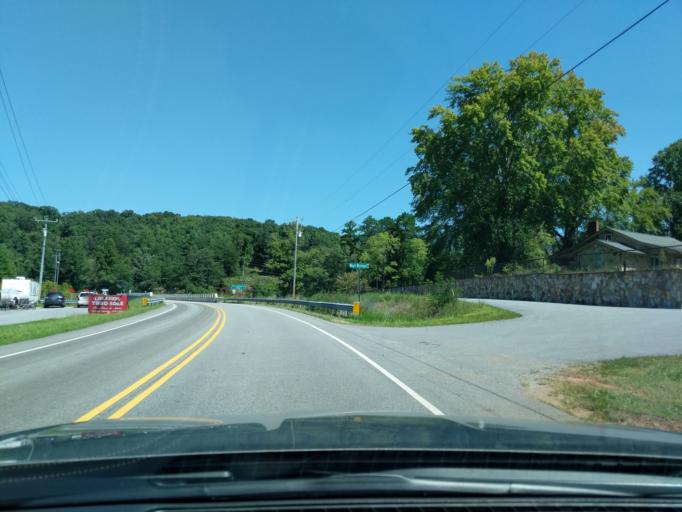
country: US
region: Georgia
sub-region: Towns County
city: Hiawassee
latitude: 35.0228
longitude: -83.7311
